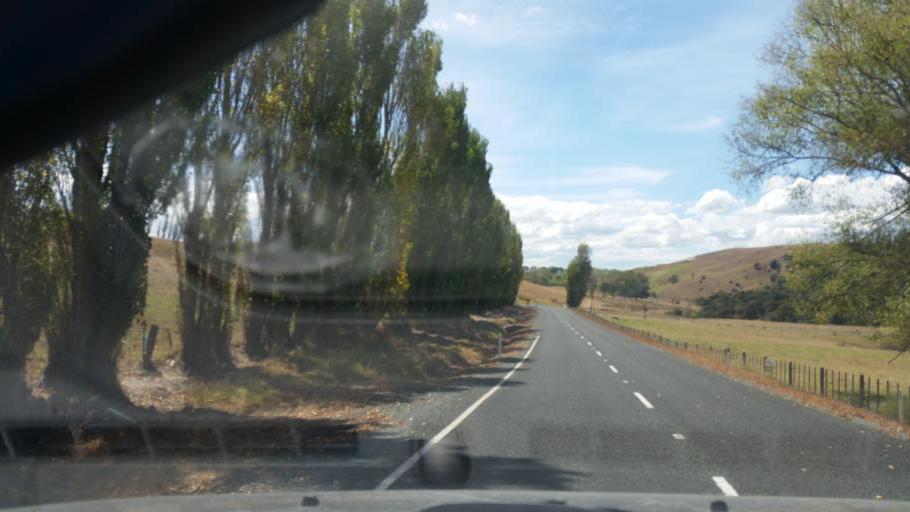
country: NZ
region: Northland
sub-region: Kaipara District
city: Dargaville
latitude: -36.1671
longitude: 174.1662
